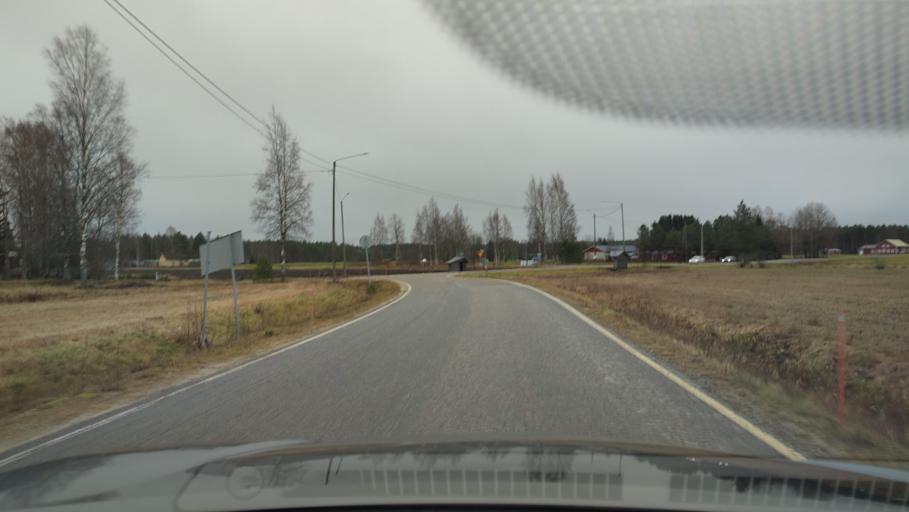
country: FI
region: Southern Ostrobothnia
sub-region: Suupohja
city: Isojoki
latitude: 62.1904
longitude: 21.9813
